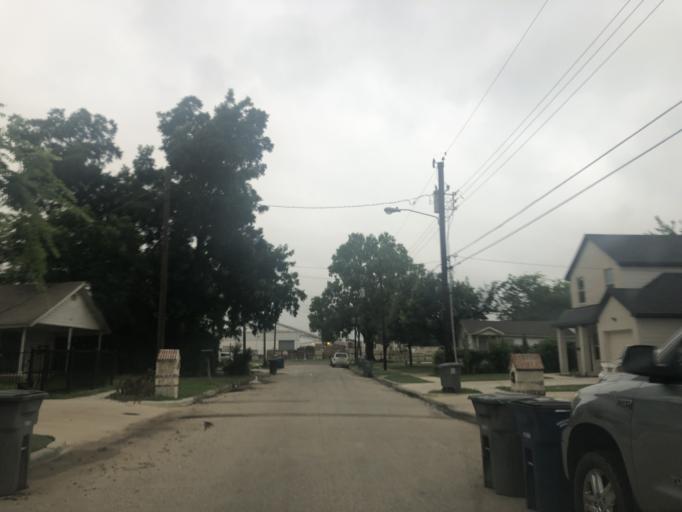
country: US
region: Texas
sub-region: Dallas County
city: Cockrell Hill
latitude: 32.7828
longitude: -96.8816
